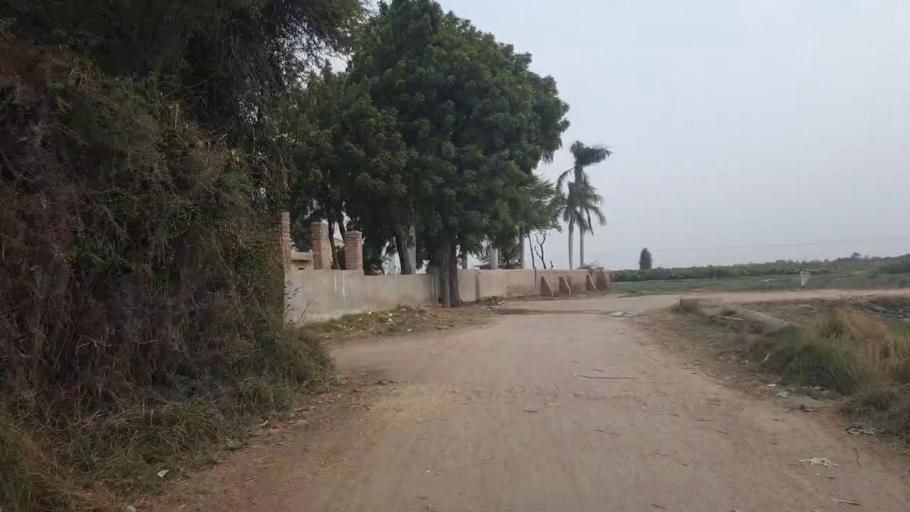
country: PK
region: Sindh
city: Shahdadpur
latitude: 25.9452
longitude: 68.7033
